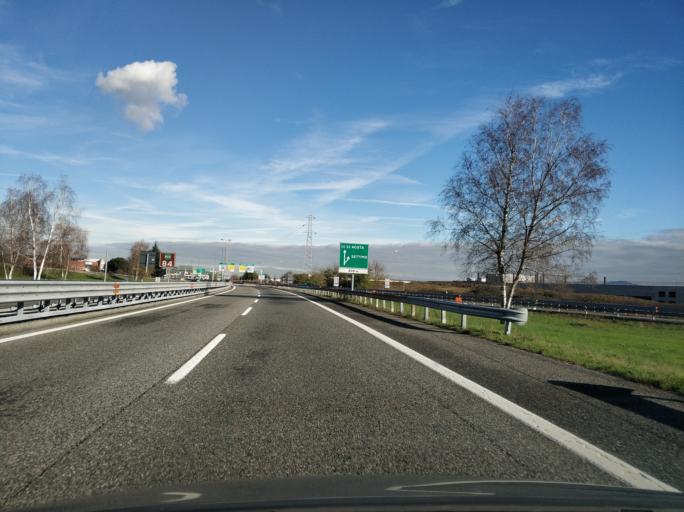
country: IT
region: Piedmont
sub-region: Provincia di Torino
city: Settimo Torinese
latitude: 45.1405
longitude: 7.7293
